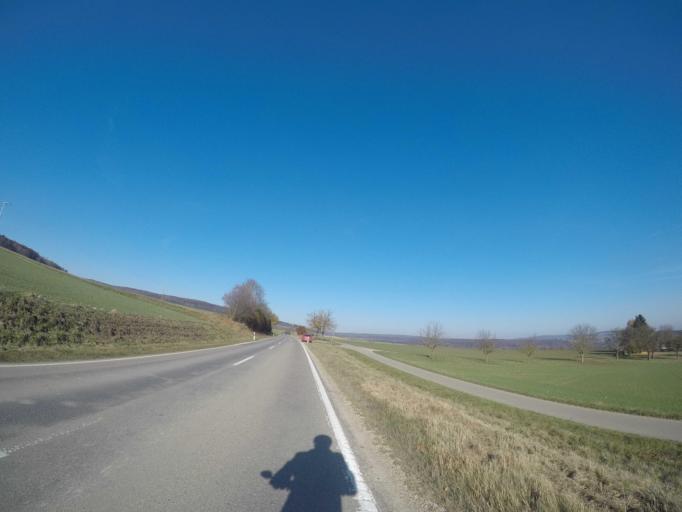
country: DE
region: Baden-Wuerttemberg
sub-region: Tuebingen Region
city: Emeringen
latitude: 48.2251
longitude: 9.5212
